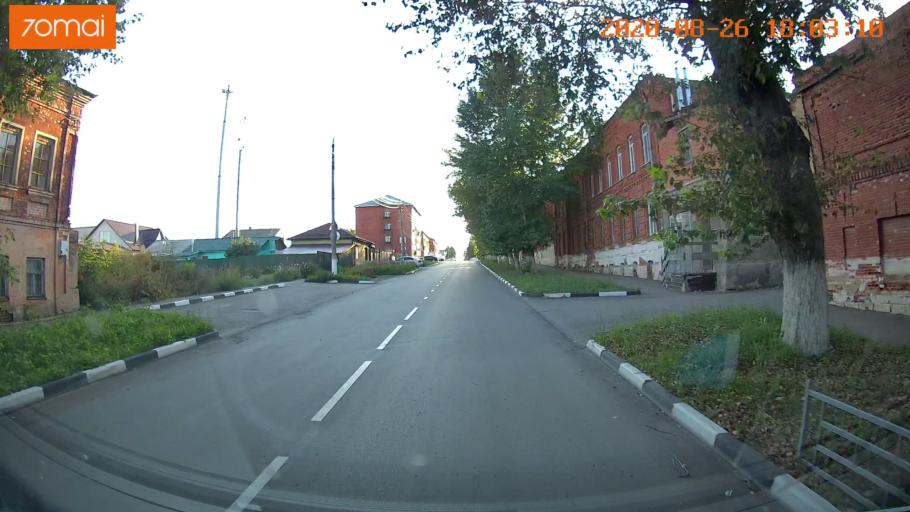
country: RU
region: Tula
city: Yefremov
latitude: 53.1415
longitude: 38.1204
